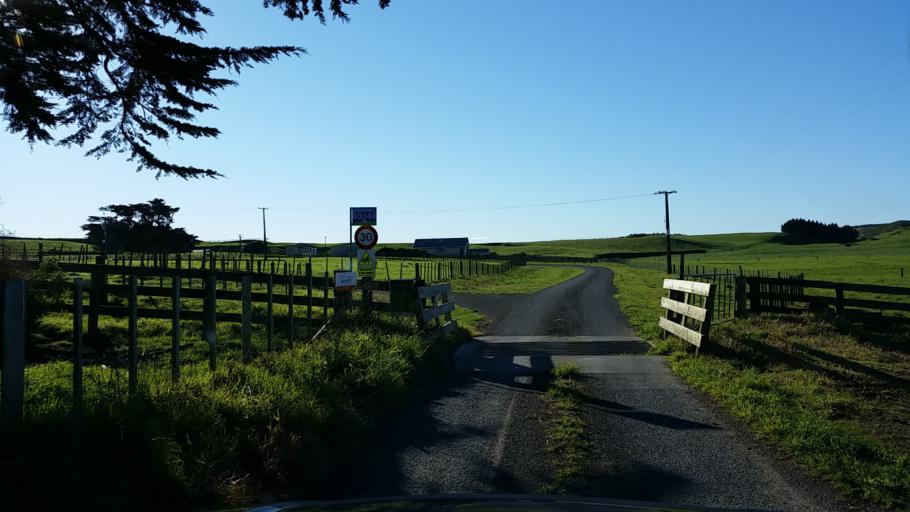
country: NZ
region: Taranaki
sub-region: South Taranaki District
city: Patea
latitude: -39.8287
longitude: 174.7059
